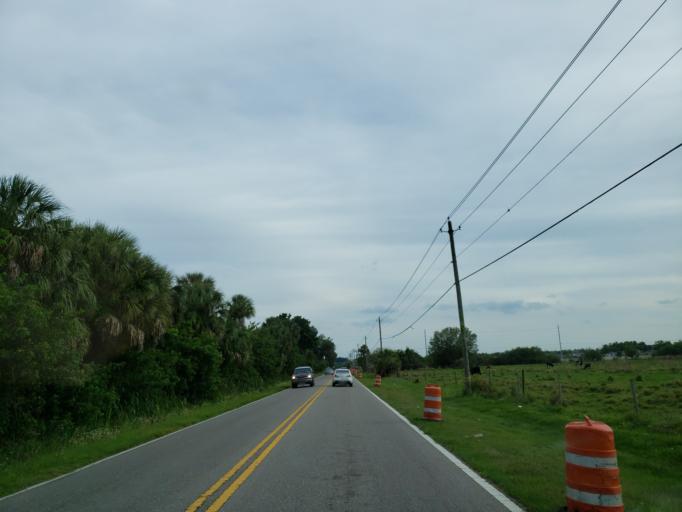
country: US
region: Florida
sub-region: Hillsborough County
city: Ruskin
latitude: 27.7380
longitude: -82.4187
